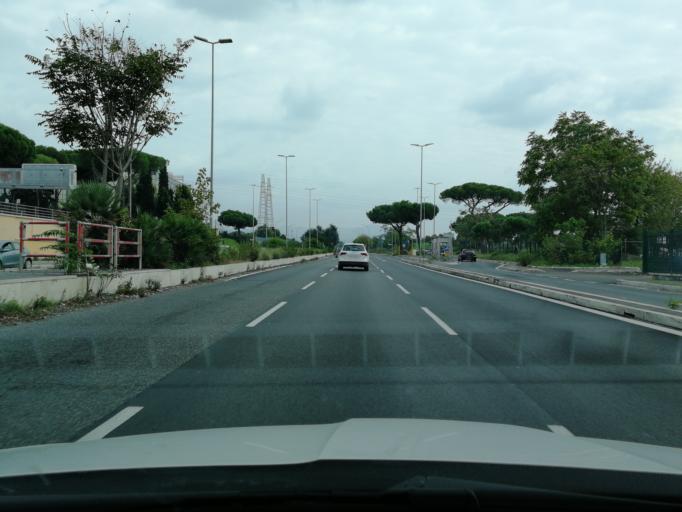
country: IT
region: Latium
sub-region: Citta metropolitana di Roma Capitale
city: Ciampino
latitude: 41.8492
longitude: 12.5744
